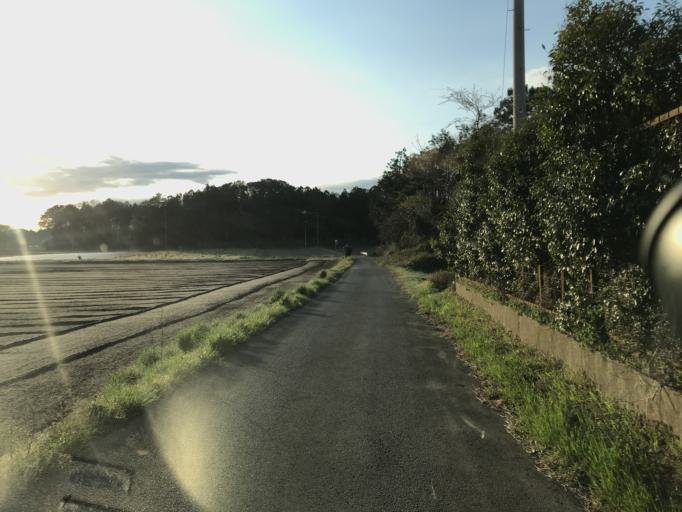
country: JP
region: Chiba
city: Omigawa
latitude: 35.7950
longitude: 140.5472
